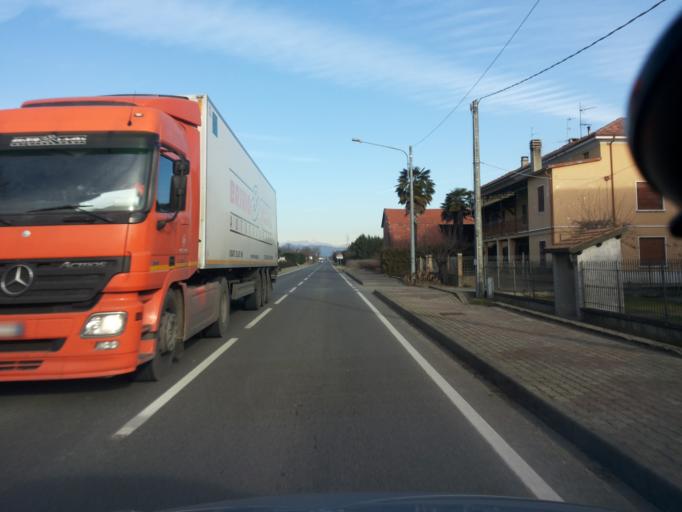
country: IT
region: Piedmont
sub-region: Provincia di Vercelli
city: Ghislarengo
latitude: 45.5361
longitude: 8.3856
